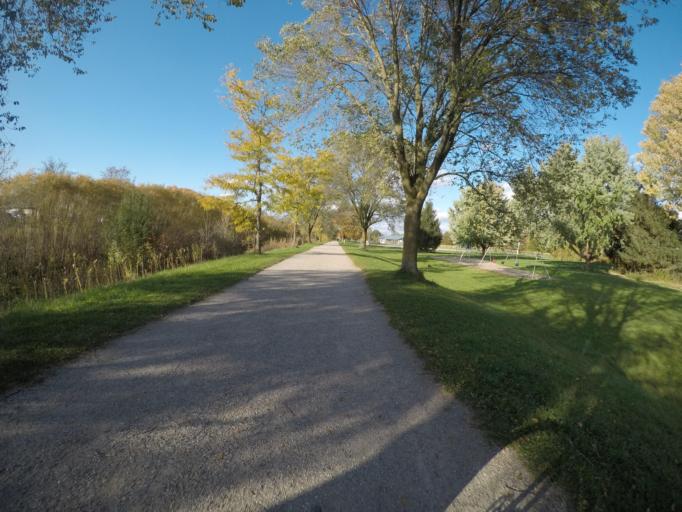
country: CA
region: Ontario
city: Kitchener
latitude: 43.4257
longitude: -80.4591
